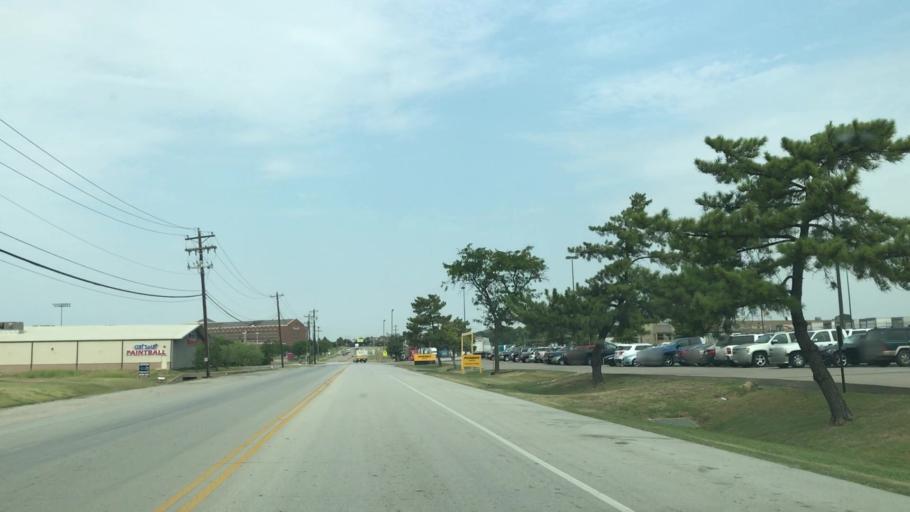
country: US
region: Texas
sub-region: Tarrant County
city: Keller
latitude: 32.9115
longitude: -97.2643
